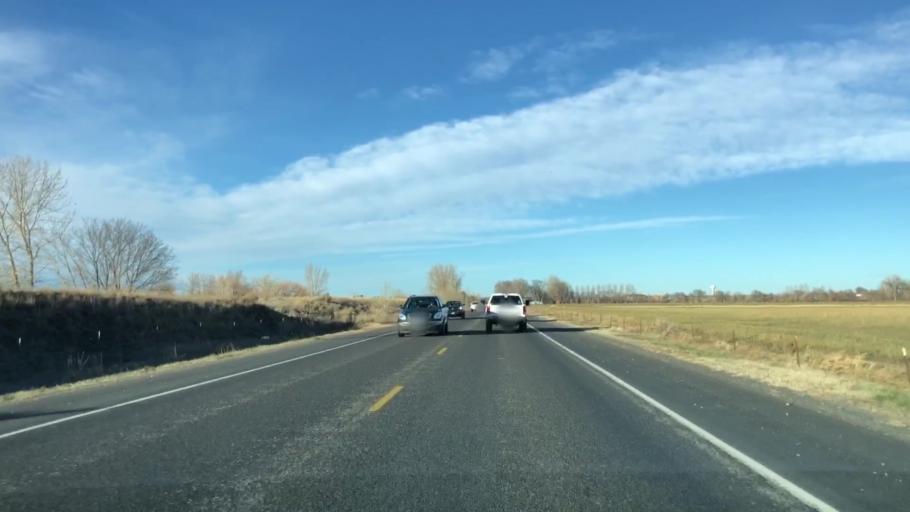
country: US
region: Colorado
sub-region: Weld County
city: Windsor
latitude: 40.5015
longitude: -104.9818
